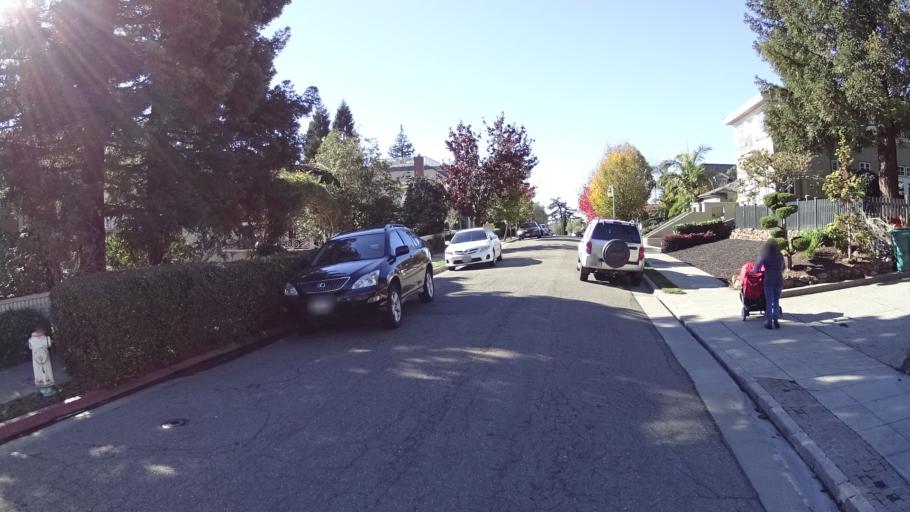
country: US
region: California
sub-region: Alameda County
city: Piedmont
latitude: 37.8441
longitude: -122.2398
